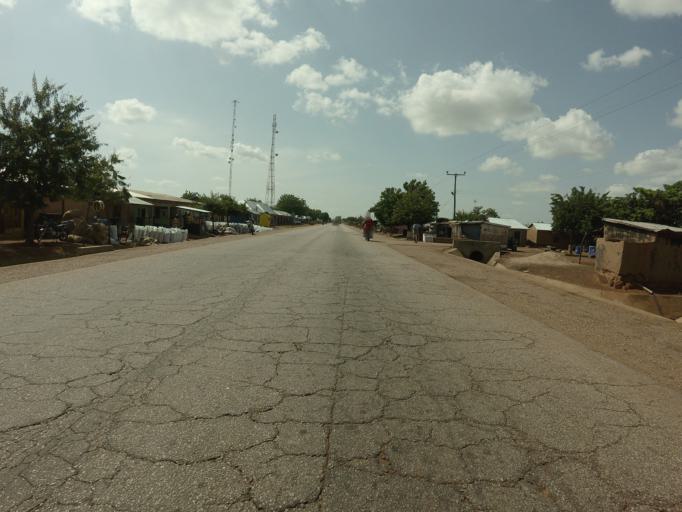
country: GH
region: Northern
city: Savelugu
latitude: 9.8703
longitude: -0.8716
